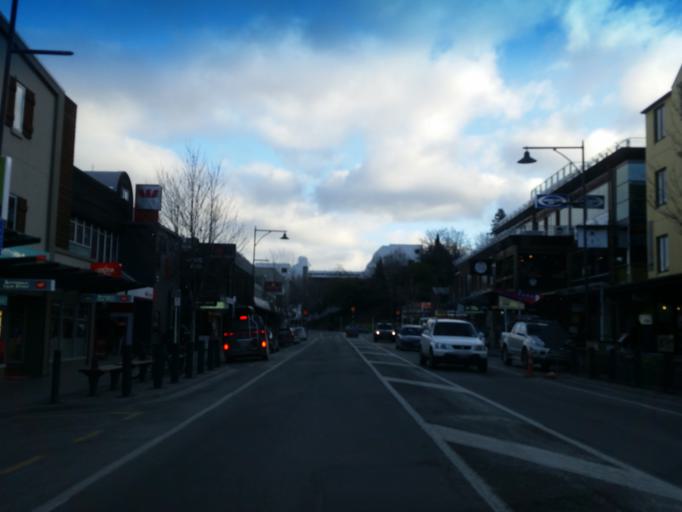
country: NZ
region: Otago
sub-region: Queenstown-Lakes District
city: Queenstown
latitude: -45.0319
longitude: 168.6589
